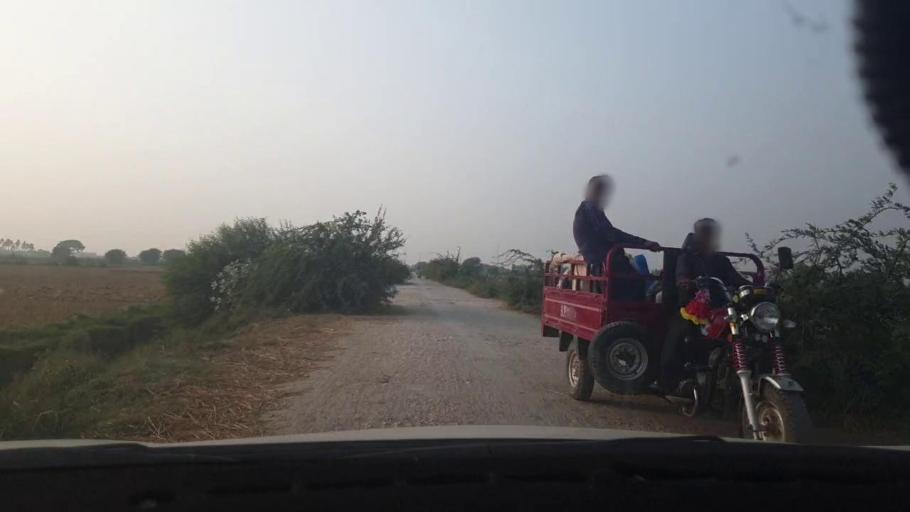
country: PK
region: Sindh
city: Bulri
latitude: 24.8514
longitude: 68.3430
